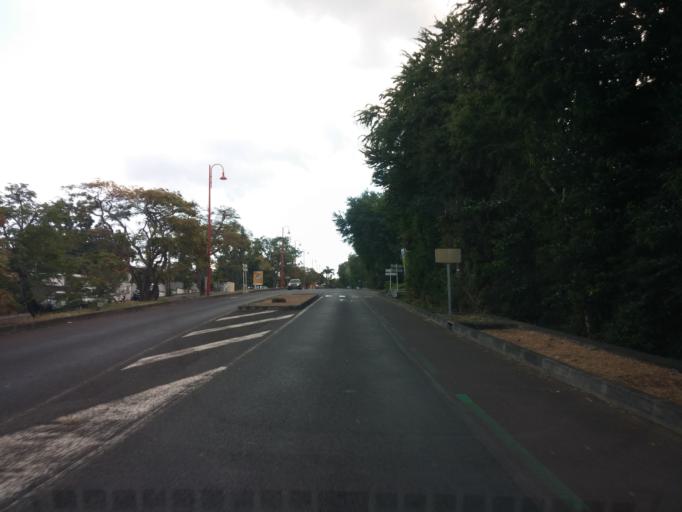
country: RE
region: Reunion
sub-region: Reunion
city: La Possession
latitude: -20.9378
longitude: 55.3323
